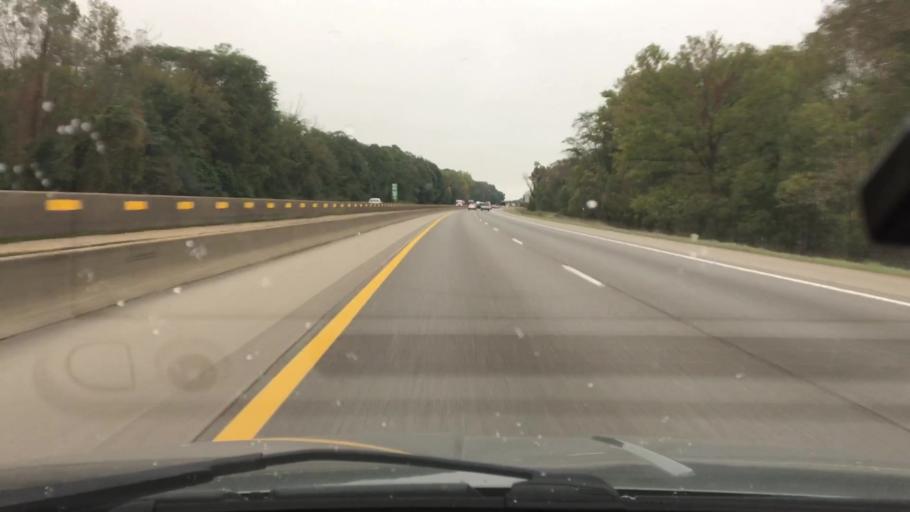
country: US
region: Michigan
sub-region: Kalamazoo County
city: Galesburg
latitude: 42.2694
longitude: -85.4565
